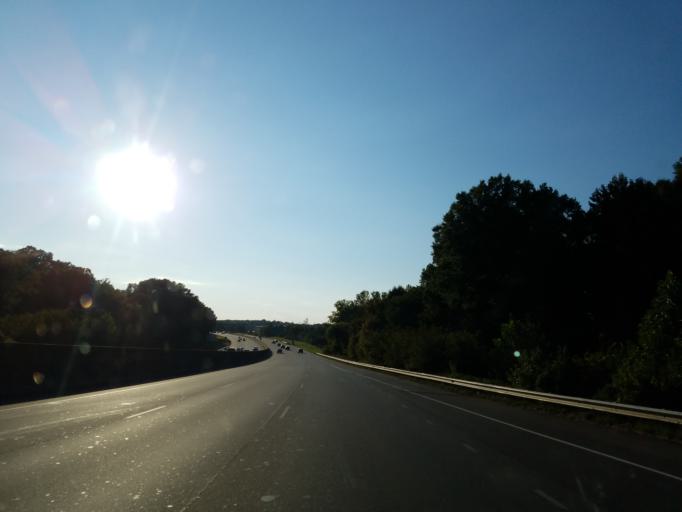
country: US
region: North Carolina
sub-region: Gaston County
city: Gastonia
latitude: 35.2856
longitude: -81.1936
